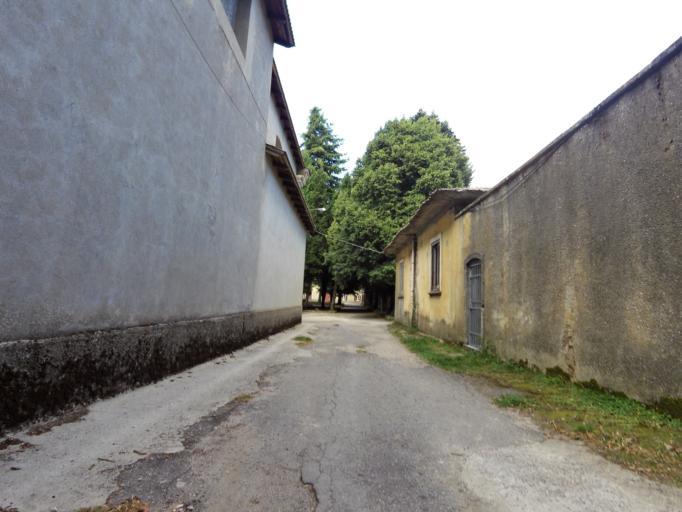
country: IT
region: Calabria
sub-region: Provincia di Vibo-Valentia
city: Nardodipace
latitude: 38.5080
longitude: 16.3795
